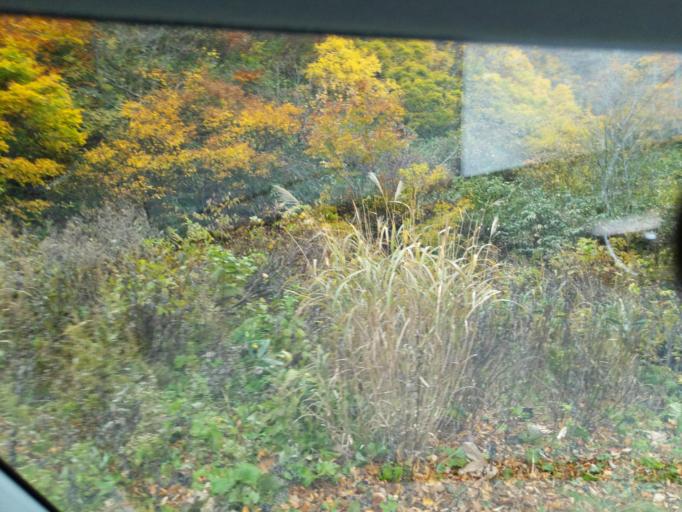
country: JP
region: Iwate
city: Mizusawa
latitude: 39.1275
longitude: 140.8253
